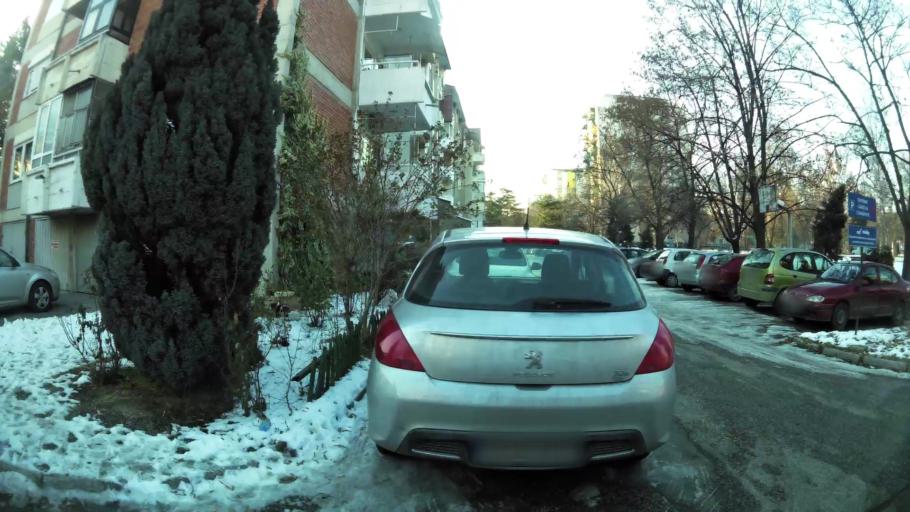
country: MK
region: Karpos
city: Skopje
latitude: 41.9945
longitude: 21.4090
